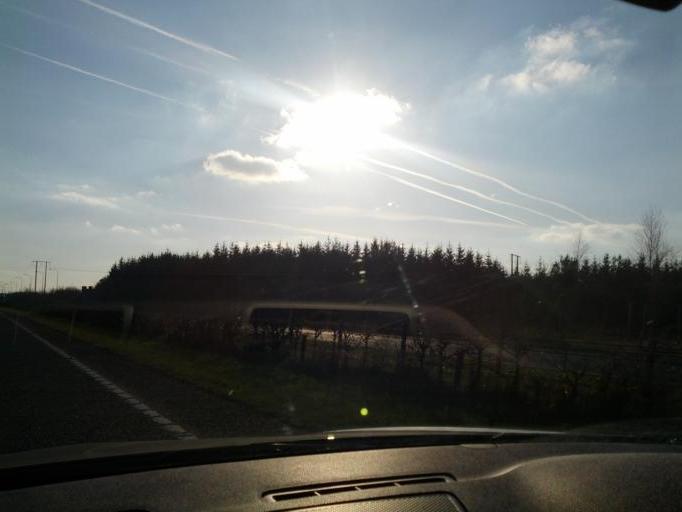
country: IE
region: Leinster
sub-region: Laois
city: Portarlington
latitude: 53.0943
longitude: -7.1648
